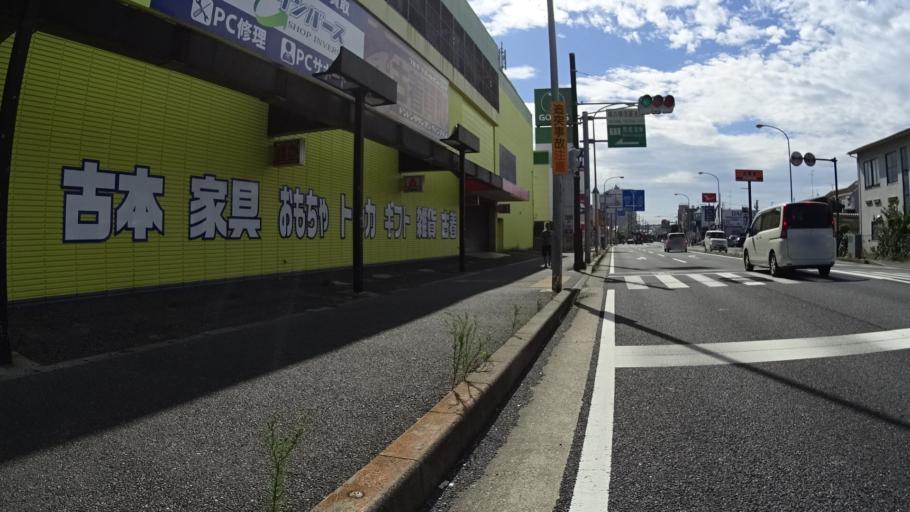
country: JP
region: Kanagawa
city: Yokosuka
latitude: 35.2645
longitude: 139.6918
